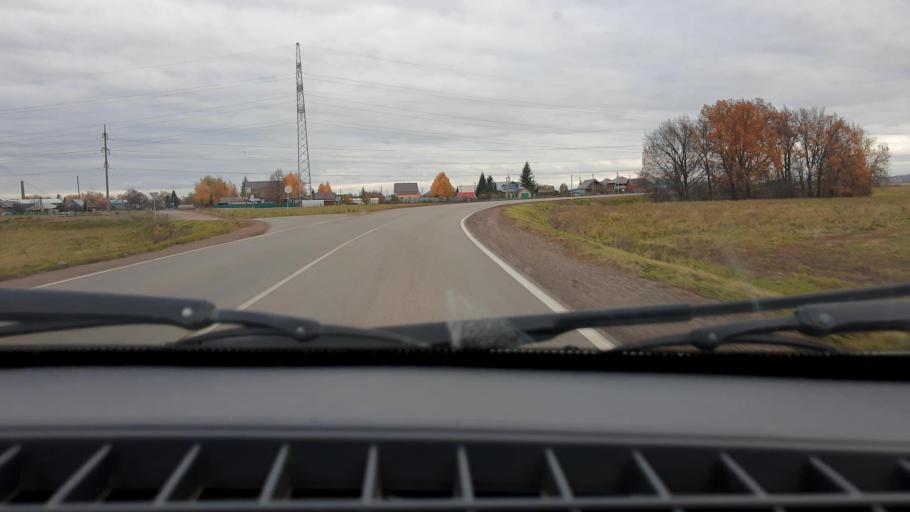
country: RU
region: Bashkortostan
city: Kabakovo
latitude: 54.5540
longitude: 56.0216
